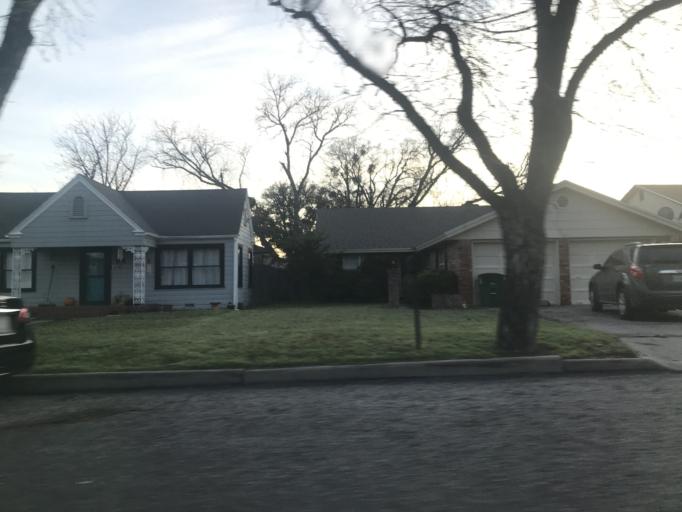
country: US
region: Texas
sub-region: Tom Green County
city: San Angelo
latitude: 31.4512
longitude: -100.4559
